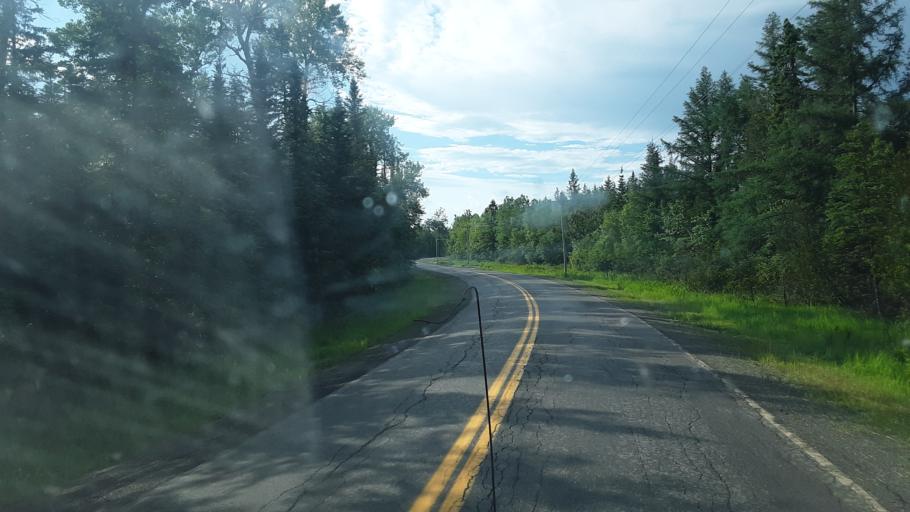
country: US
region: Maine
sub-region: Washington County
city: Calais
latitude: 45.1899
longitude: -67.5202
